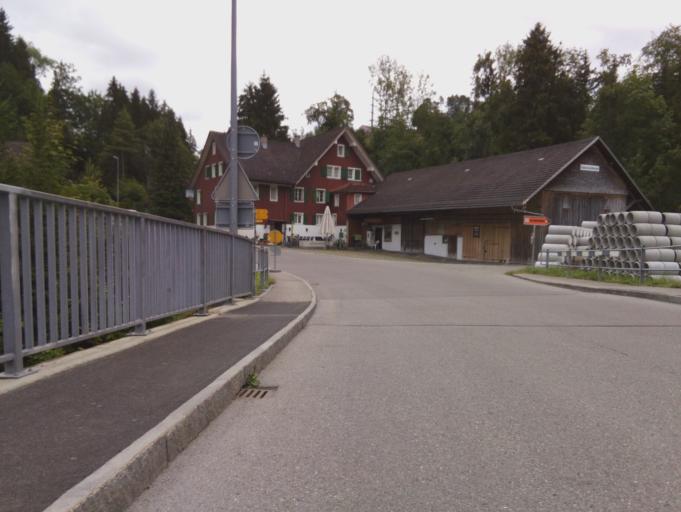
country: CH
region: Saint Gallen
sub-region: Wahlkreis Wil
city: Jonschwil
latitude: 47.4103
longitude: 9.0783
